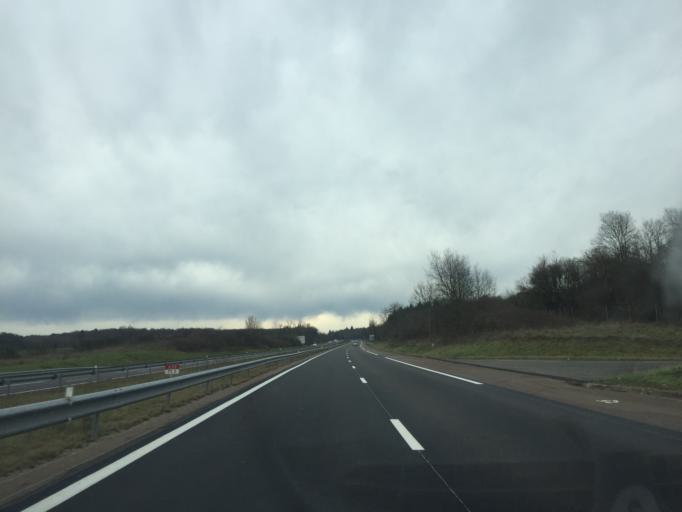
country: FR
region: Franche-Comte
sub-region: Departement du Jura
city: Bletterans
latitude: 46.8011
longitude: 5.5322
